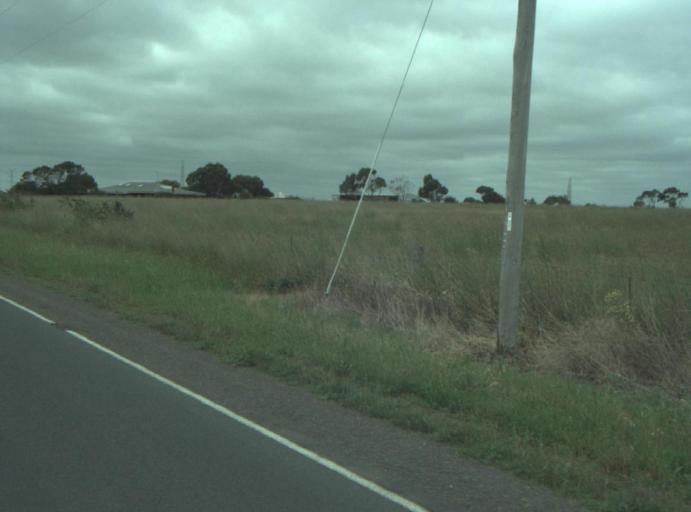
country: AU
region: Victoria
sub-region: Greater Geelong
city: Bell Post Hill
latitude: -38.0277
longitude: 144.2897
